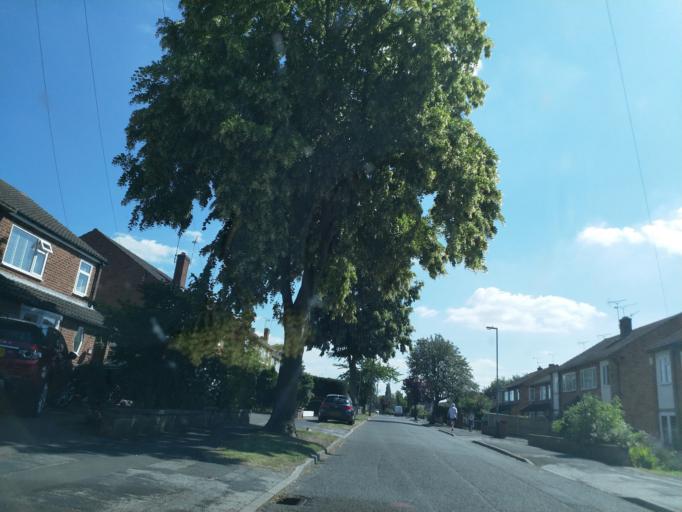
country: GB
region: England
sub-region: Warwickshire
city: Kenilworth
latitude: 52.3422
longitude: -1.5716
